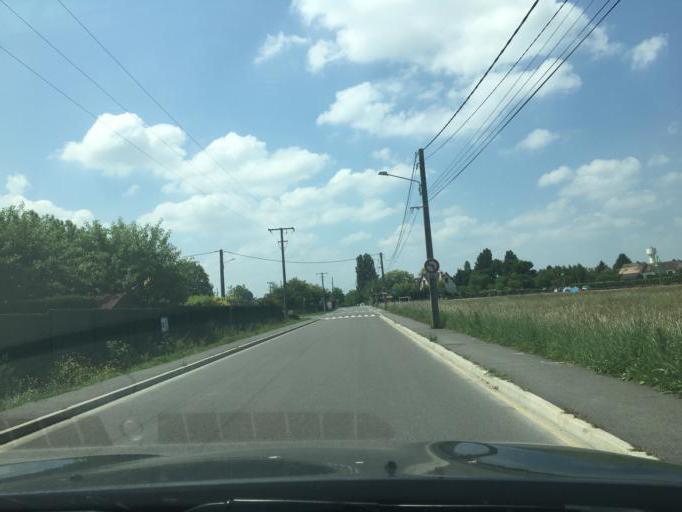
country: FR
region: Centre
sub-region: Departement du Loiret
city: Trainou
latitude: 47.9750
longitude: 2.1090
